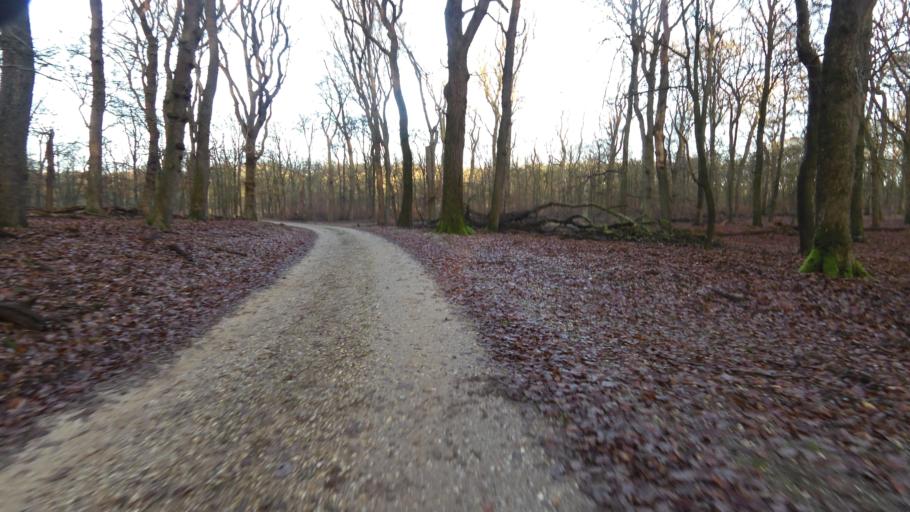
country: NL
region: Gelderland
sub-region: Gemeente Apeldoorn
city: Uddel
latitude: 52.2222
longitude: 5.8454
